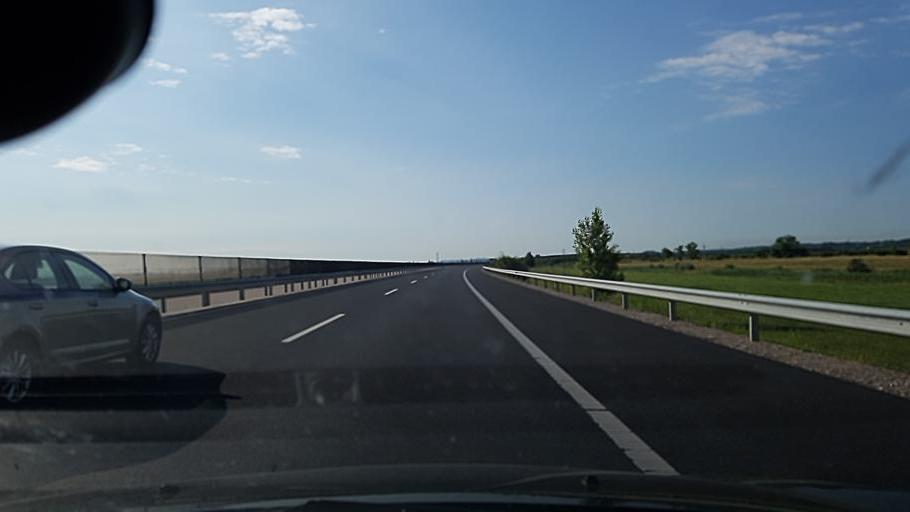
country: HU
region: Fejer
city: Adony
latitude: 47.1203
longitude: 18.8323
